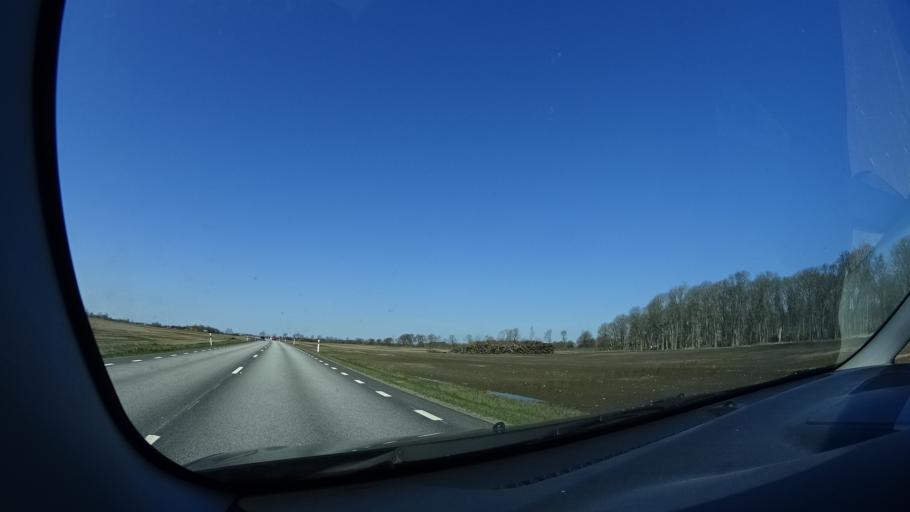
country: SE
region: Skane
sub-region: Angelholms Kommun
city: Strovelstorp
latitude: 56.2077
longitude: 12.7568
